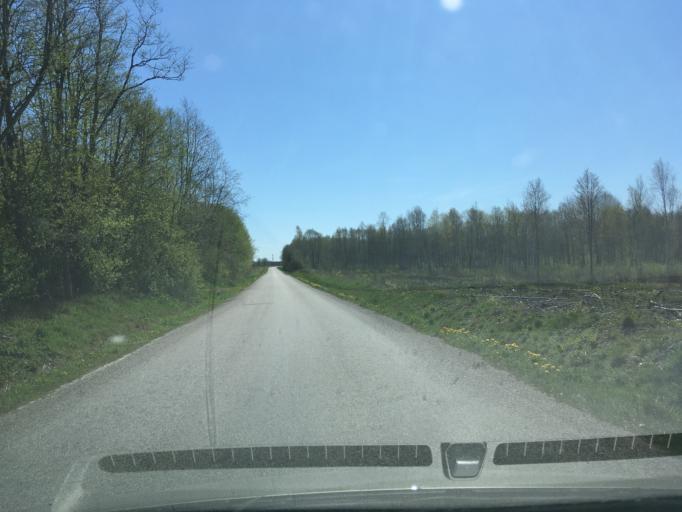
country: EE
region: Harju
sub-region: Raasiku vald
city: Arukula
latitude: 59.4032
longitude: 25.0773
